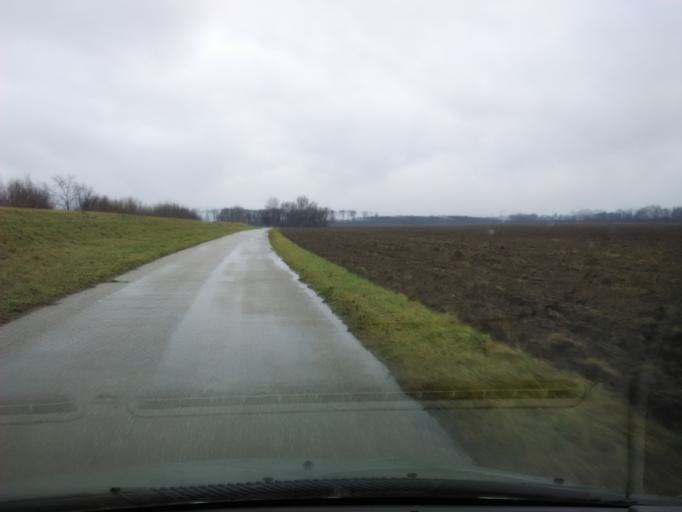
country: SK
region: Nitriansky
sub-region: Okres Nitra
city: Vrable
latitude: 48.2353
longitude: 18.2839
